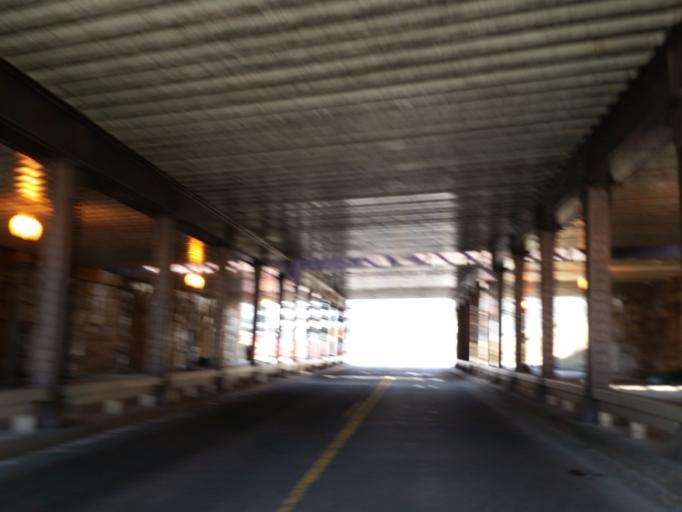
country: US
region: Washington, D.C.
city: Washington, D.C.
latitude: 38.9038
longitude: -77.0035
